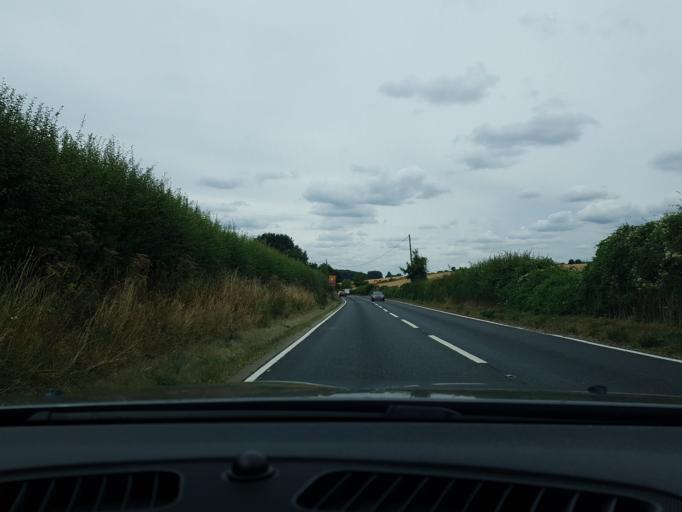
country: GB
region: England
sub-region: Hampshire
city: Tadley
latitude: 51.2928
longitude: -1.1685
